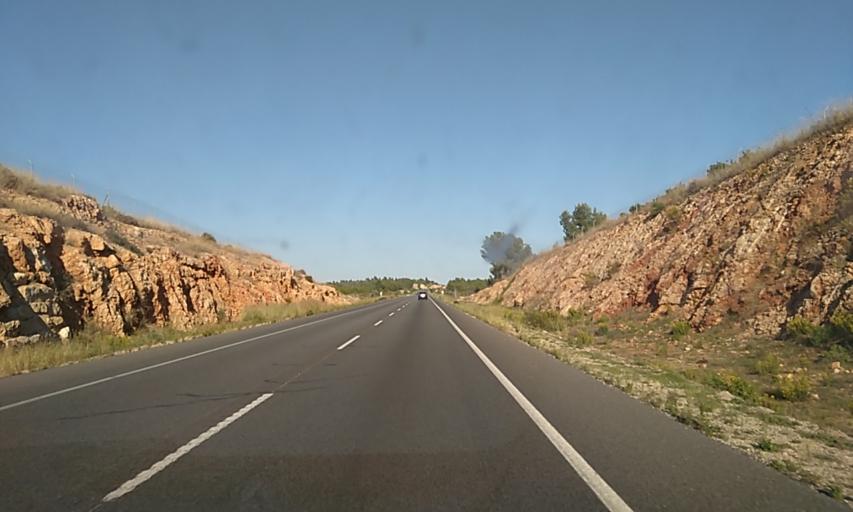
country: ES
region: Valencia
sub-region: Provincia de Castello
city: Torreblanca
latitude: 40.2159
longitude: 0.1540
